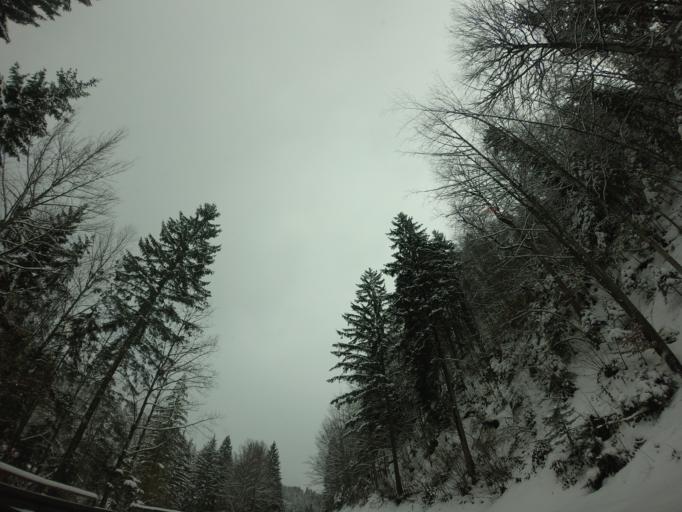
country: DE
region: Bavaria
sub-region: Upper Bavaria
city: Grainau
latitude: 47.4832
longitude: 11.0331
